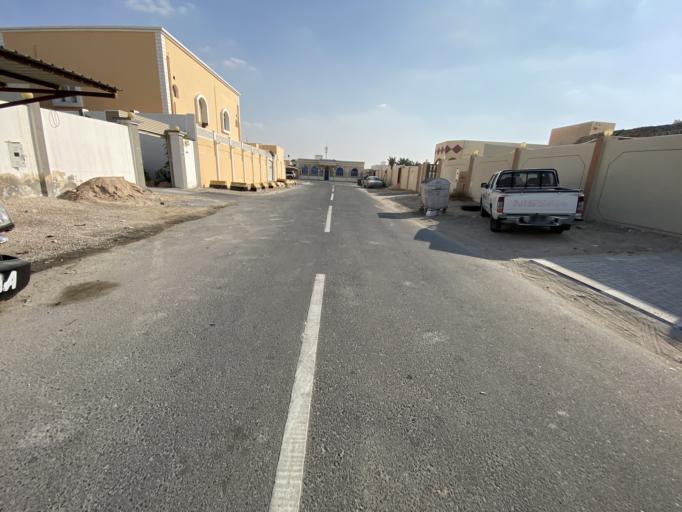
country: QA
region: Baladiyat ar Rayyan
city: Ar Rayyan
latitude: 25.2332
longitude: 51.3756
